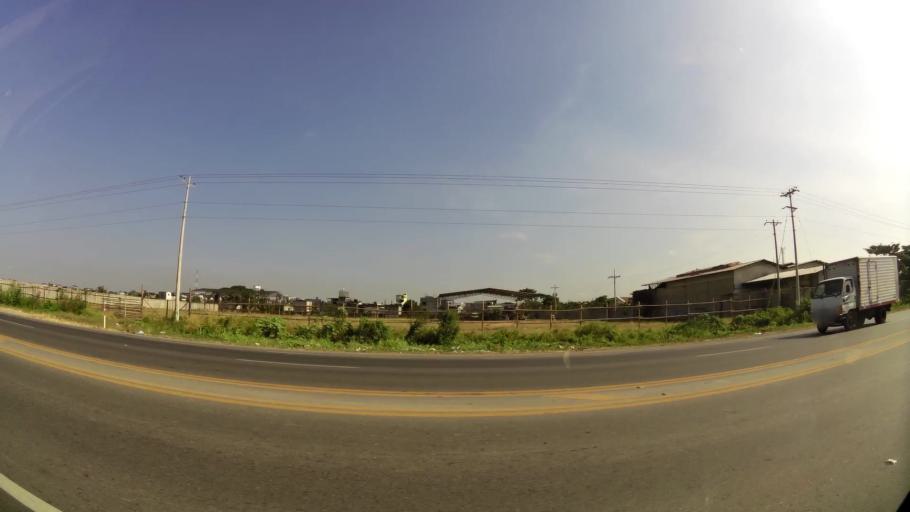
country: EC
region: Guayas
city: Eloy Alfaro
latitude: -2.1752
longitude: -79.8001
